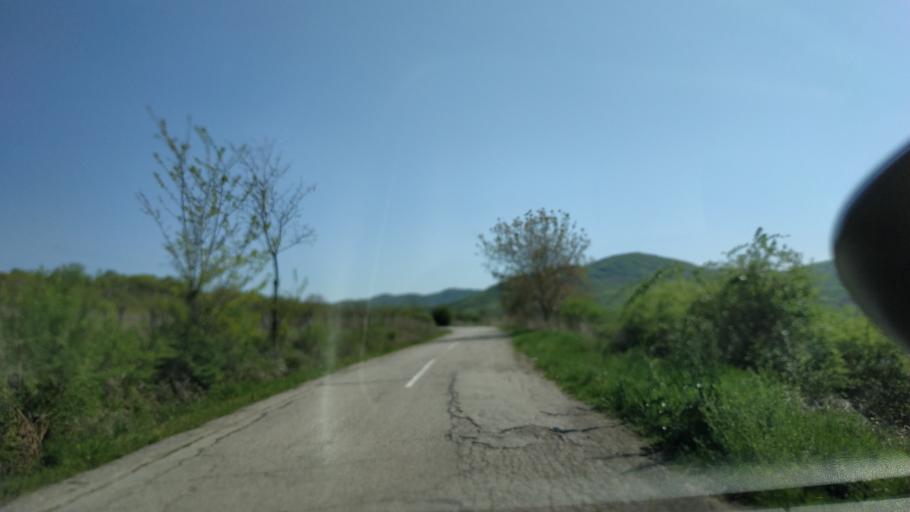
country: RS
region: Central Serbia
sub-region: Nisavski Okrug
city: Nis
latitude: 43.4383
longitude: 21.8468
